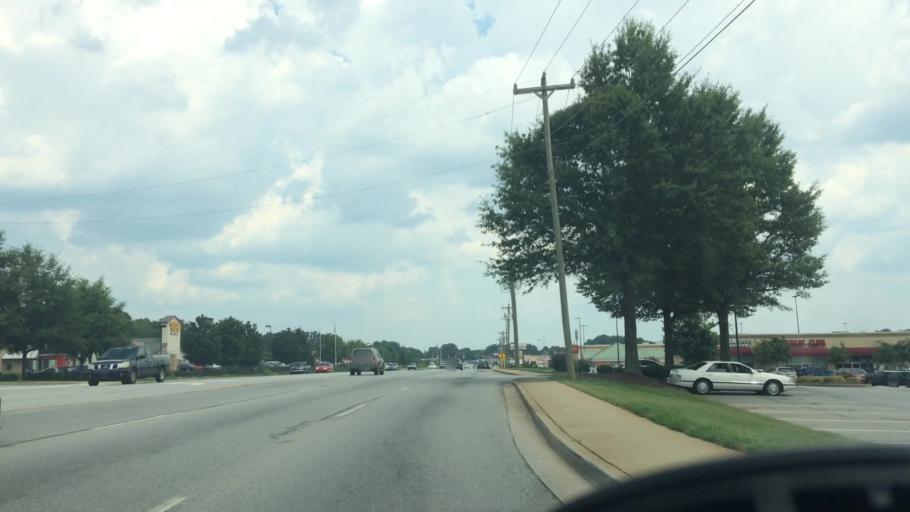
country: US
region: South Carolina
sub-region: Greenville County
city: Sans Souci
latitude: 34.8910
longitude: -82.4029
